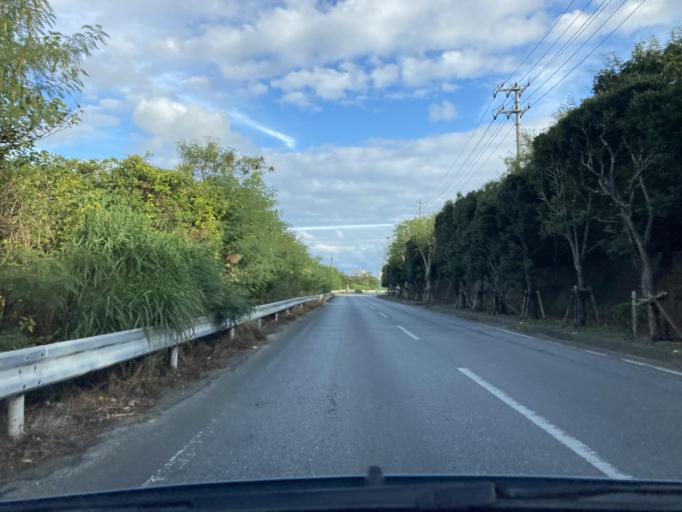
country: JP
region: Okinawa
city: Itoman
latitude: 26.1332
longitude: 127.7528
